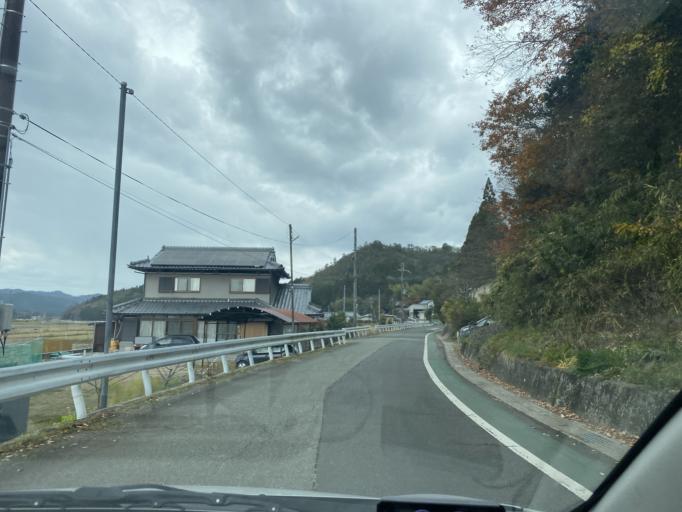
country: JP
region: Kyoto
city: Kameoka
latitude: 35.0490
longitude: 135.4791
